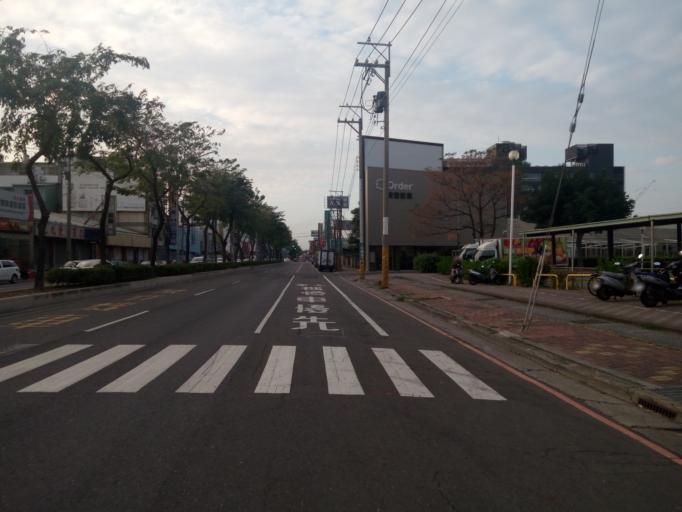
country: TW
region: Taiwan
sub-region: Chiayi
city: Jiayi Shi
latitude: 23.4811
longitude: 120.4286
